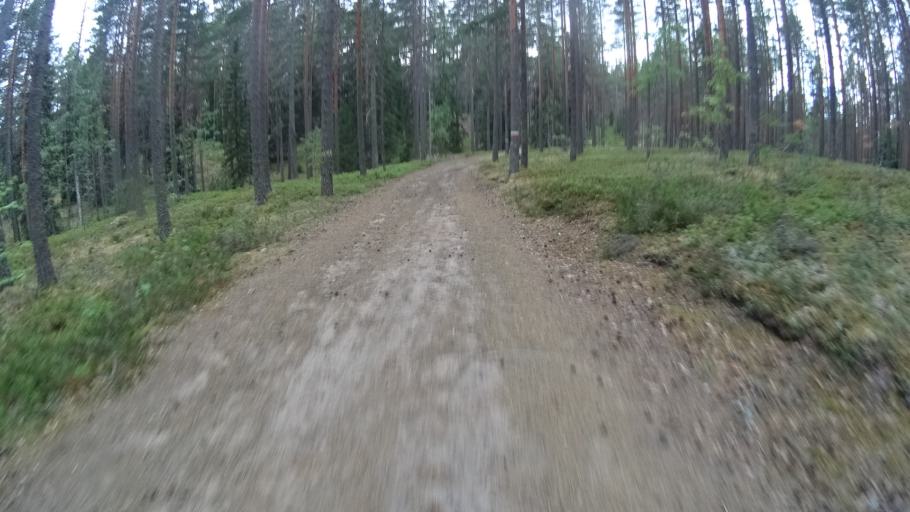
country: FI
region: Satakunta
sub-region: Pohjois-Satakunta
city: Jaemijaervi
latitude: 61.7693
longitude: 22.7565
